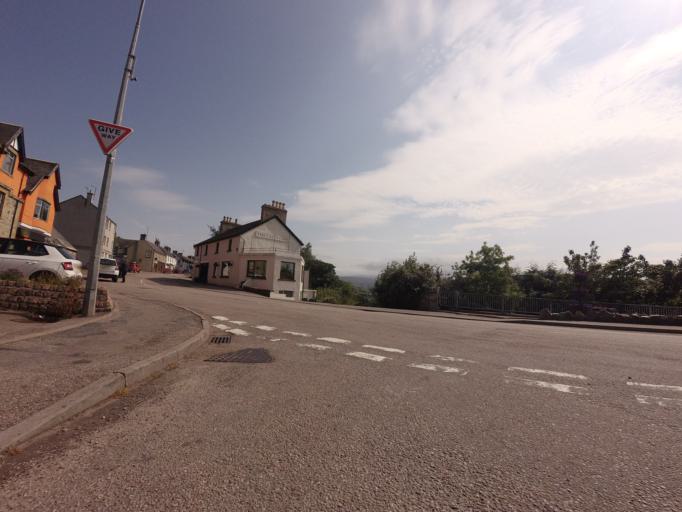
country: GB
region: Scotland
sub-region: Highland
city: Alness
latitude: 57.8917
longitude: -4.3463
